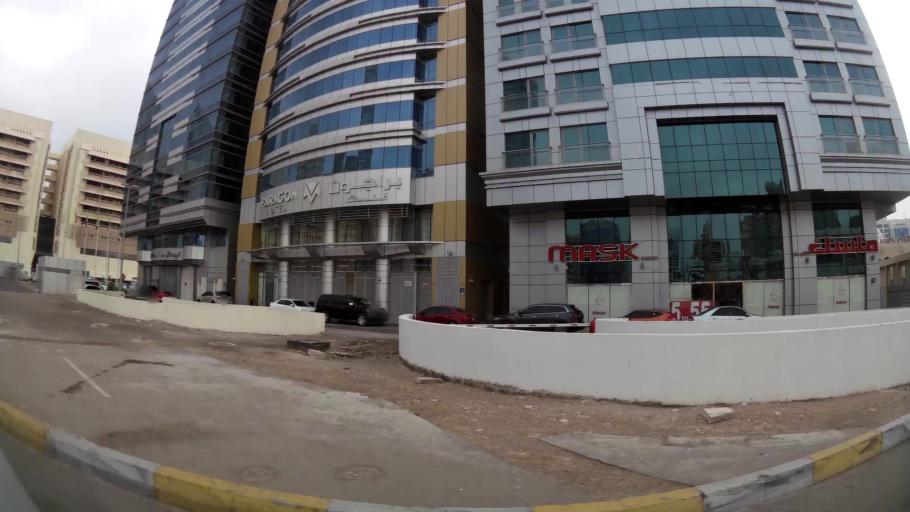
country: AE
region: Abu Dhabi
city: Abu Dhabi
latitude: 24.4843
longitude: 54.3639
